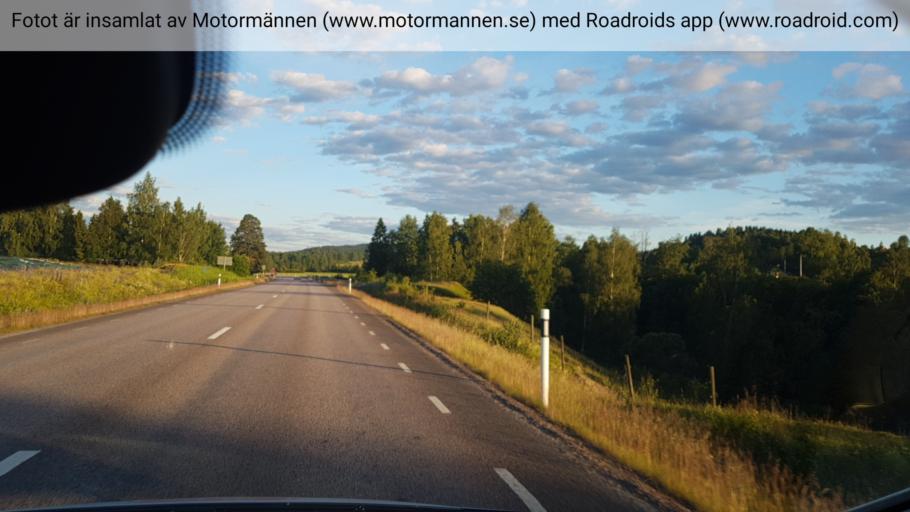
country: SE
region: Vaermland
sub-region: Sunne Kommun
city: Sunne
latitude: 59.9597
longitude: 13.1075
